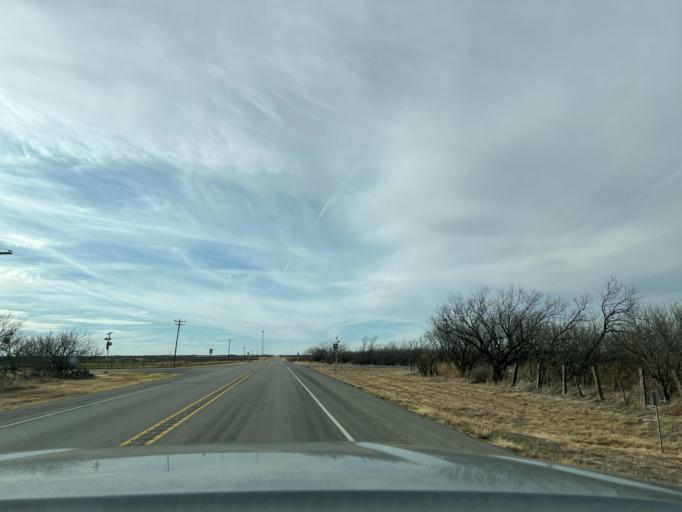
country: US
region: Texas
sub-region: Jones County
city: Anson
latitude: 32.7507
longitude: -99.7125
